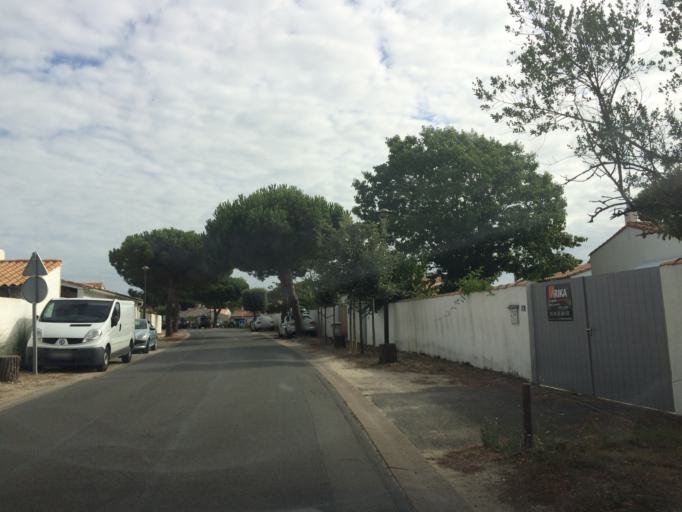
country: FR
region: Poitou-Charentes
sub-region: Departement de la Charente-Maritime
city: La Flotte
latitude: 46.1889
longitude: -1.3342
